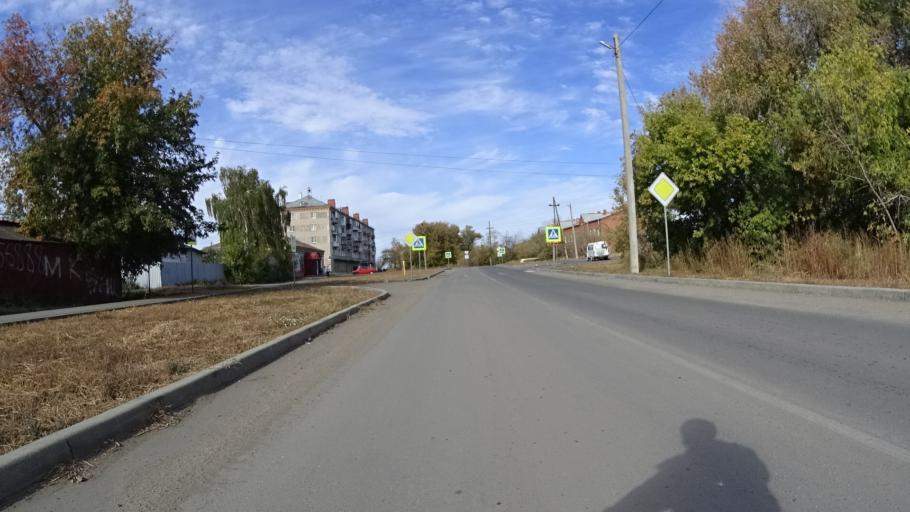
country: RU
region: Chelyabinsk
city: Troitsk
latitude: 54.0772
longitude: 61.5858
